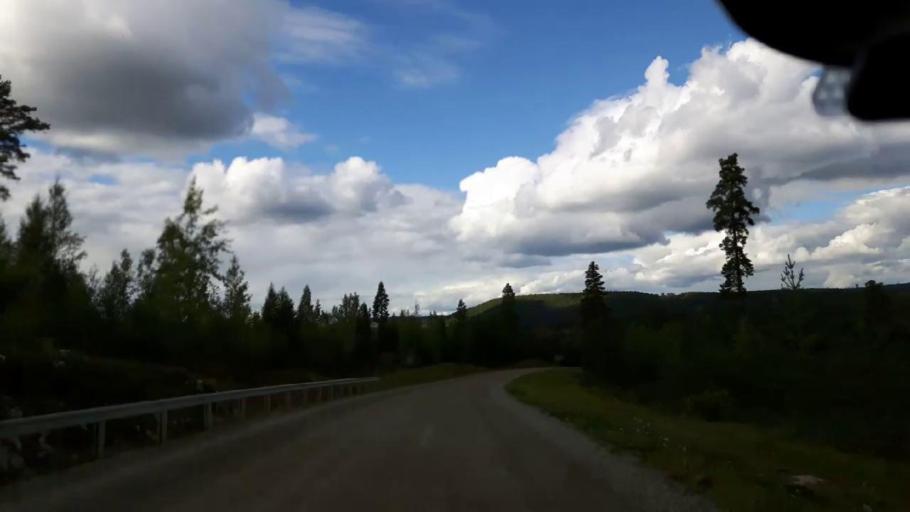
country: SE
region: Jaemtland
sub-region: Stroemsunds Kommun
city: Stroemsund
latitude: 63.4061
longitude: 15.5638
